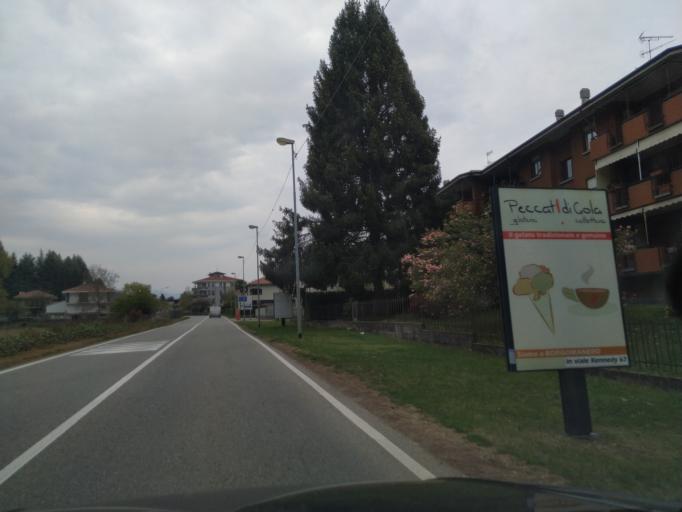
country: IT
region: Piedmont
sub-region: Provincia di Novara
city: Borgomanero
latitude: 45.6934
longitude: 8.4544
